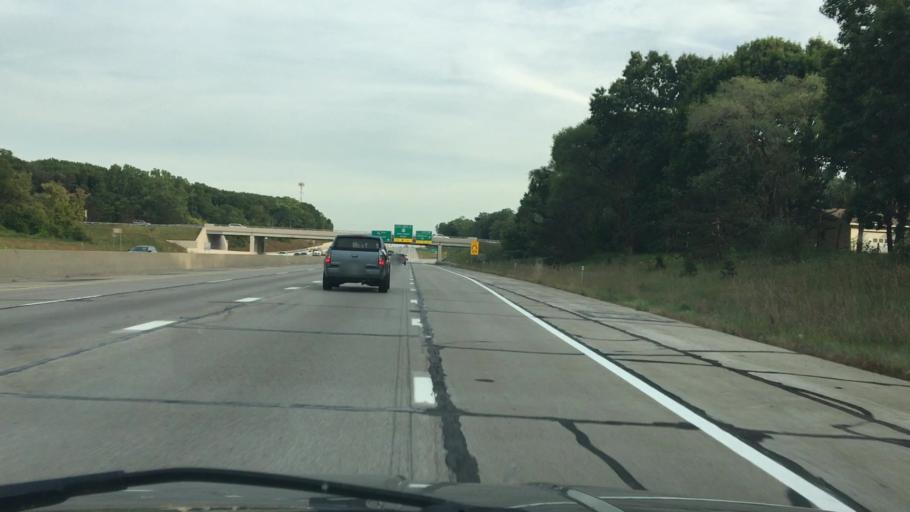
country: US
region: Michigan
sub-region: Livingston County
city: Brighton
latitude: 42.5340
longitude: -83.7680
